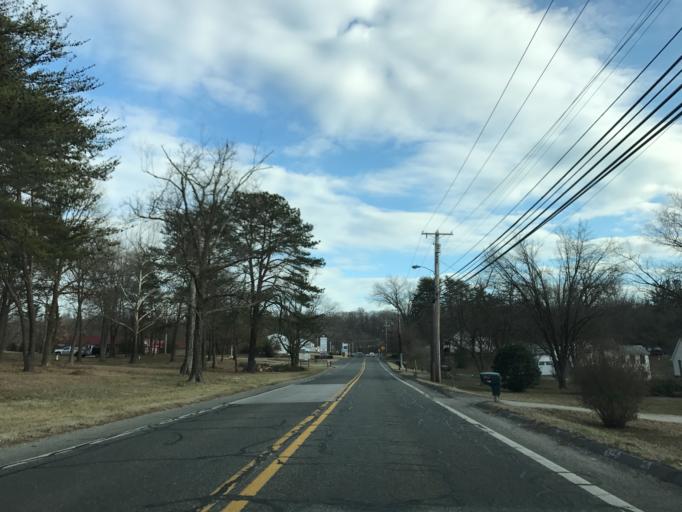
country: US
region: Maryland
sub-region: Anne Arundel County
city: Crownsville
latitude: 39.0551
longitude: -76.6216
